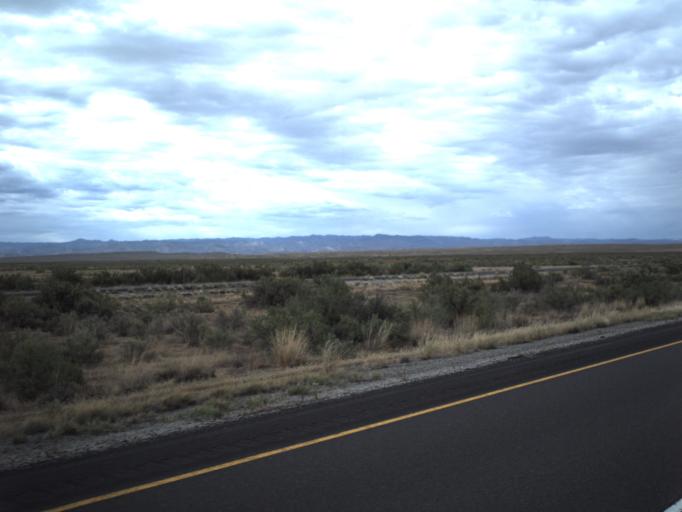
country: US
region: Colorado
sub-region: Mesa County
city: Loma
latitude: 39.0742
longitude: -109.2344
